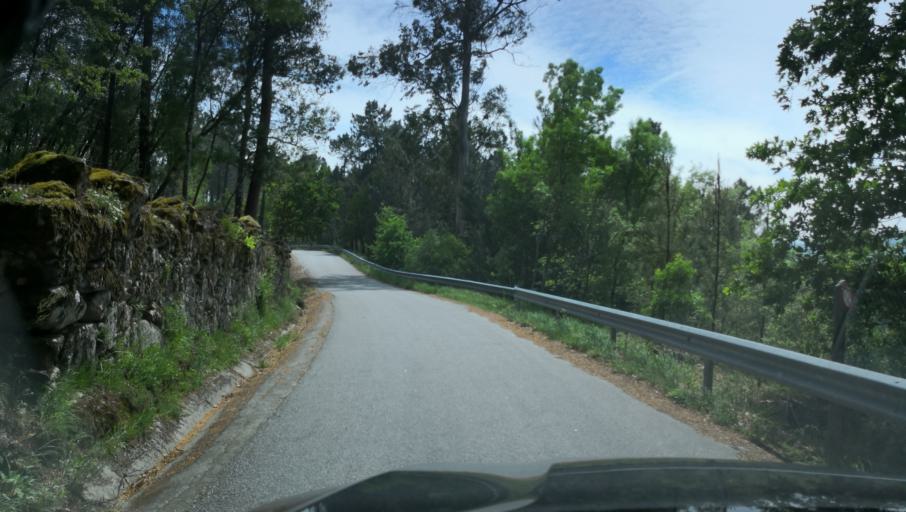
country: PT
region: Vila Real
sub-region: Vila Real
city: Vila Real
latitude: 41.3189
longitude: -7.7903
